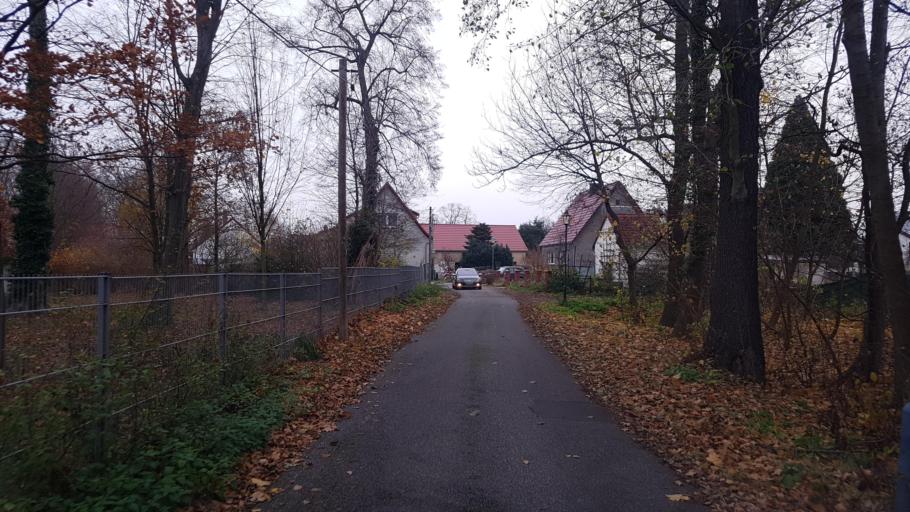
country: DE
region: Brandenburg
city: Lauchhammer
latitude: 51.4662
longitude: 13.7457
